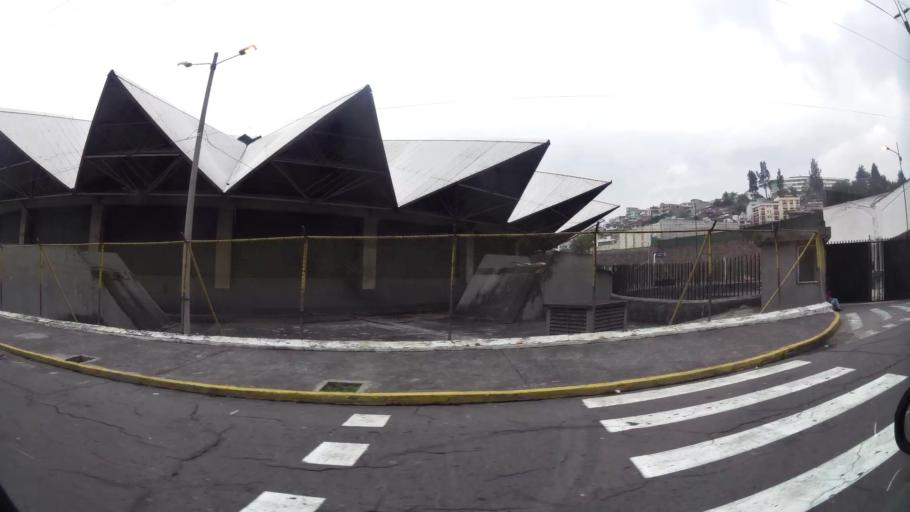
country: EC
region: Pichincha
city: Quito
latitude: -0.2127
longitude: -78.4903
